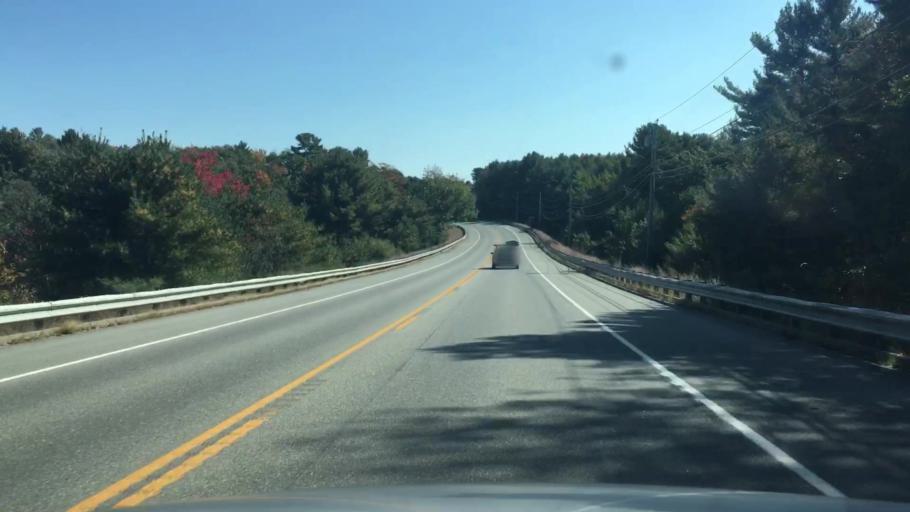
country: US
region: Maine
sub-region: Androscoggin County
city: Lisbon Falls
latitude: 43.9650
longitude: -70.0175
